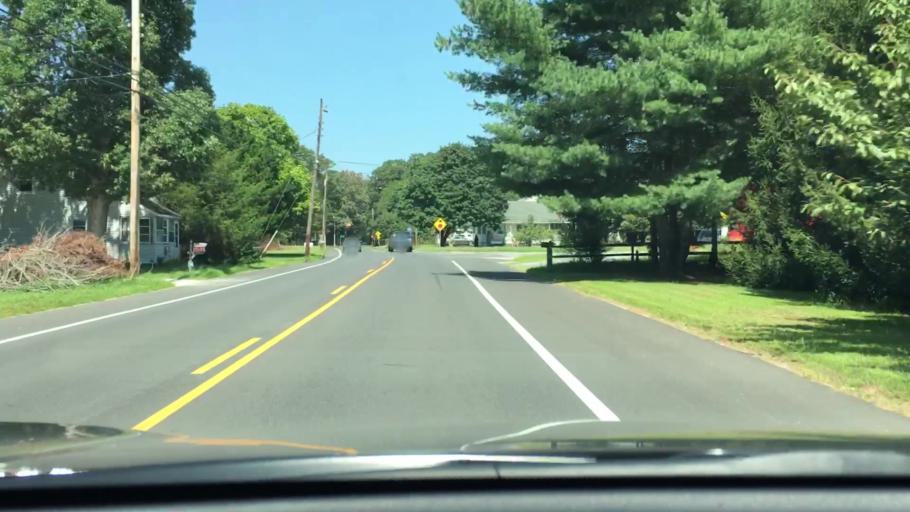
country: US
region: New Jersey
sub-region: Cape May County
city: Woodbine
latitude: 39.2671
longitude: -74.8647
